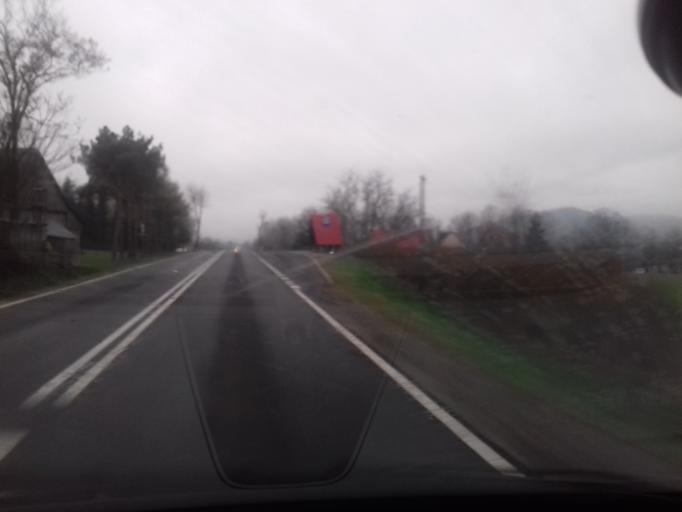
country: PL
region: Lesser Poland Voivodeship
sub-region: Powiat limanowski
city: Tymbark
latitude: 49.7275
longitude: 20.2899
